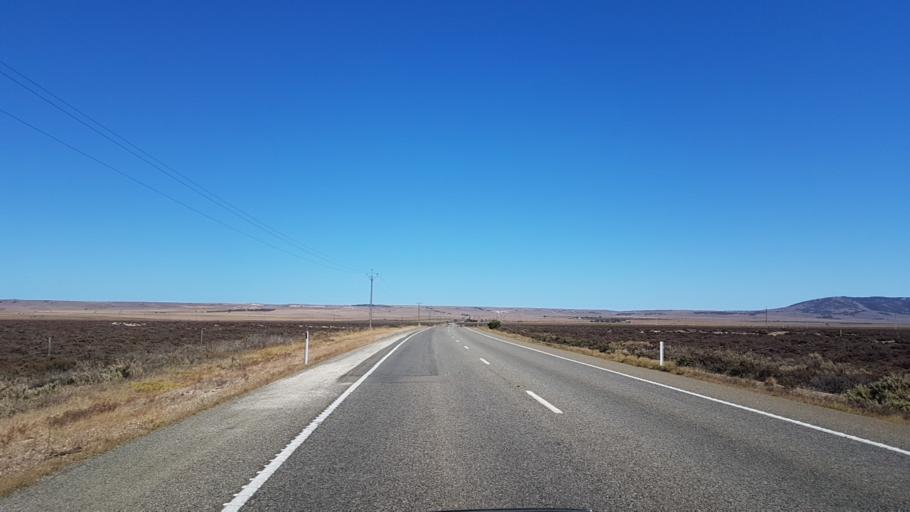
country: AU
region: South Australia
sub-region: Wakefield
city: Balaklava
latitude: -34.1010
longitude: 138.1068
